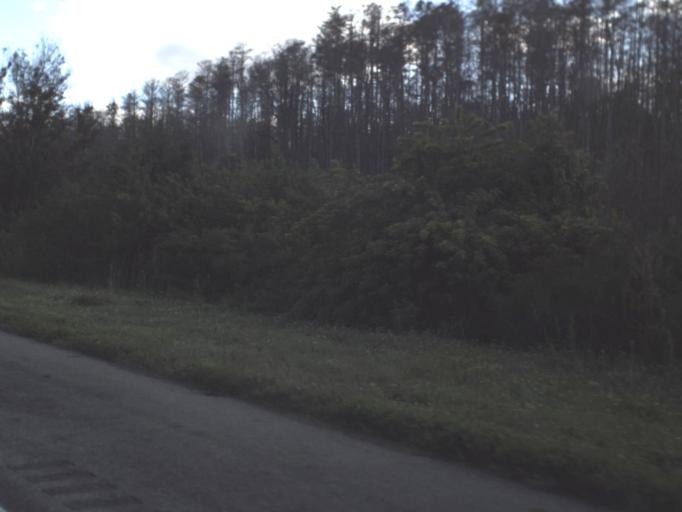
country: US
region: Florida
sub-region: Osceola County
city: Saint Cloud
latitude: 28.0905
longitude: -81.2712
